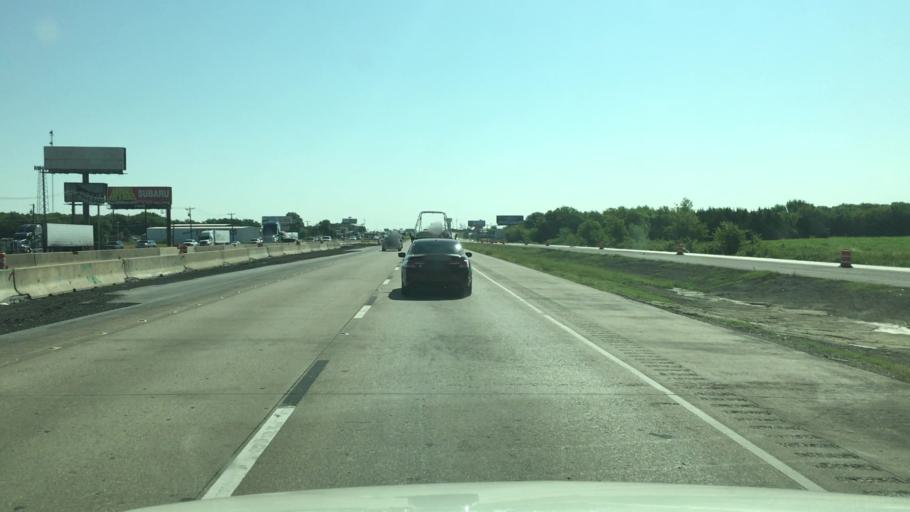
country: US
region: Texas
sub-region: Rockwall County
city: Fate
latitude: 32.9211
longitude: -96.4120
